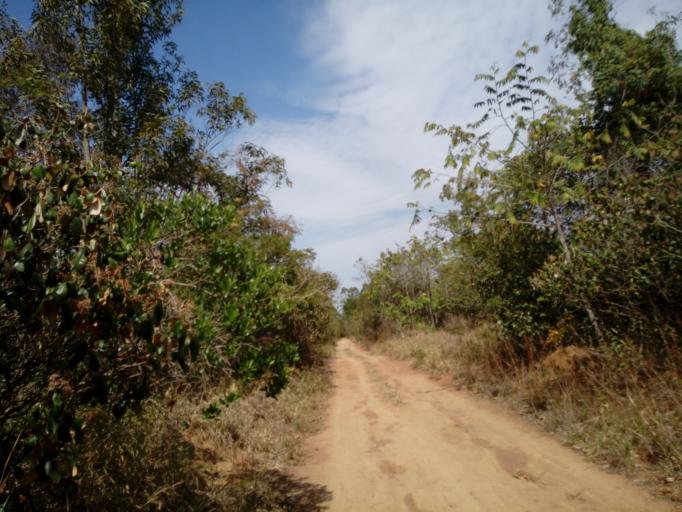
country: BR
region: Sao Paulo
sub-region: Sao Carlos
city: Sao Carlos
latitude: -21.9732
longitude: -47.8822
